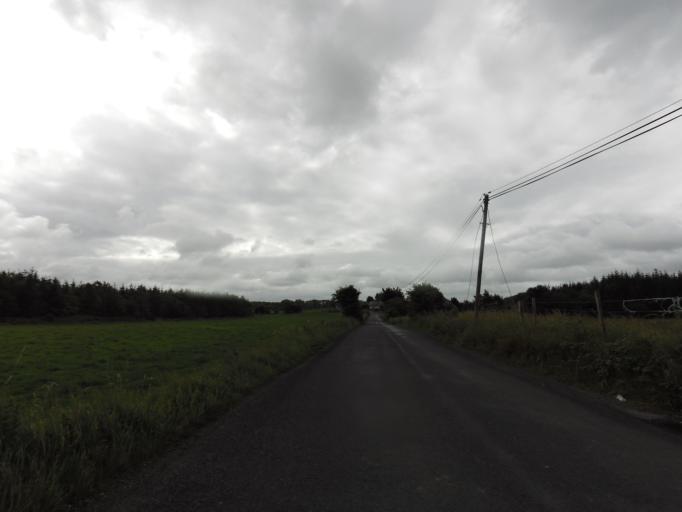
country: IE
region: Connaught
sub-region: County Galway
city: Athenry
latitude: 53.2893
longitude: -8.6934
